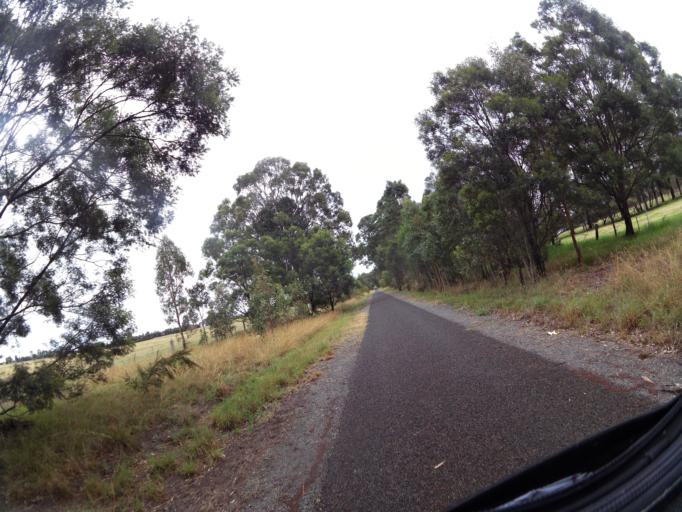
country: AU
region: Victoria
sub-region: East Gippsland
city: Bairnsdale
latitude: -37.8223
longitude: 147.7106
